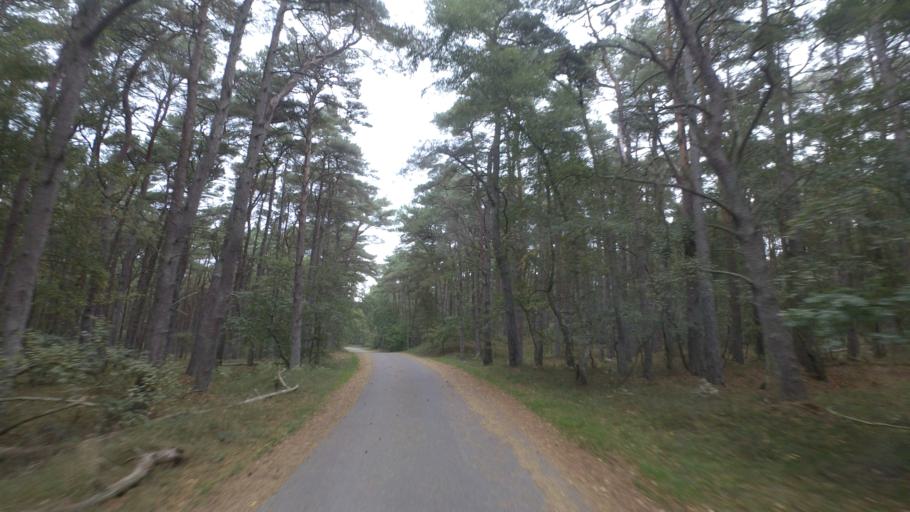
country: DK
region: Capital Region
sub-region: Bornholm Kommune
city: Nexo
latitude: 54.9988
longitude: 15.0389
